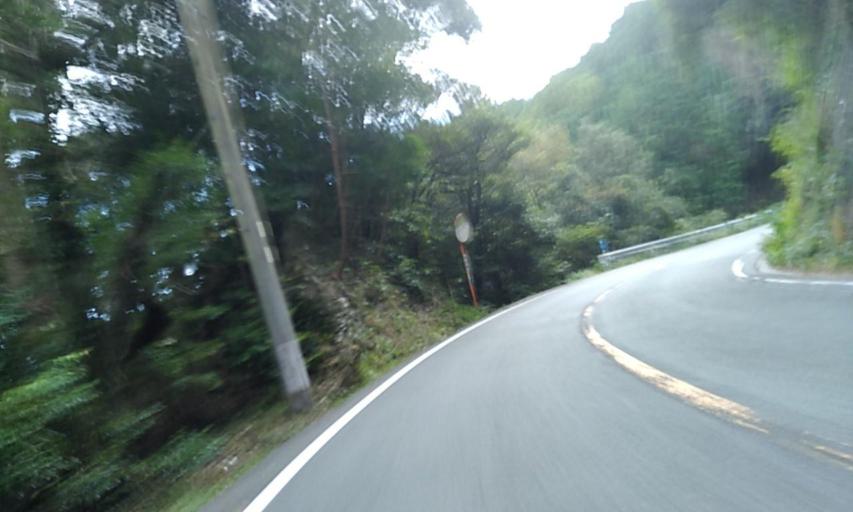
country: JP
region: Mie
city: Ise
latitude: 34.2897
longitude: 136.5348
